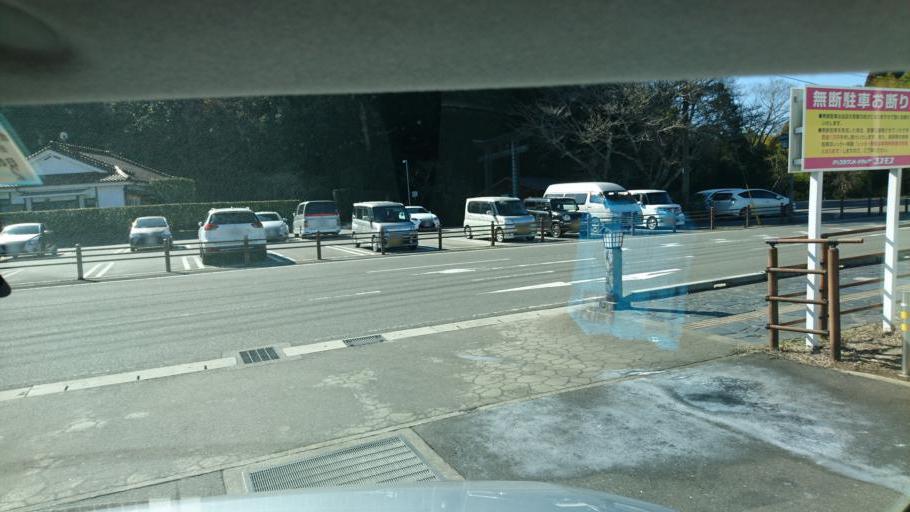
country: JP
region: Oita
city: Takedamachi
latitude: 32.7069
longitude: 131.3033
